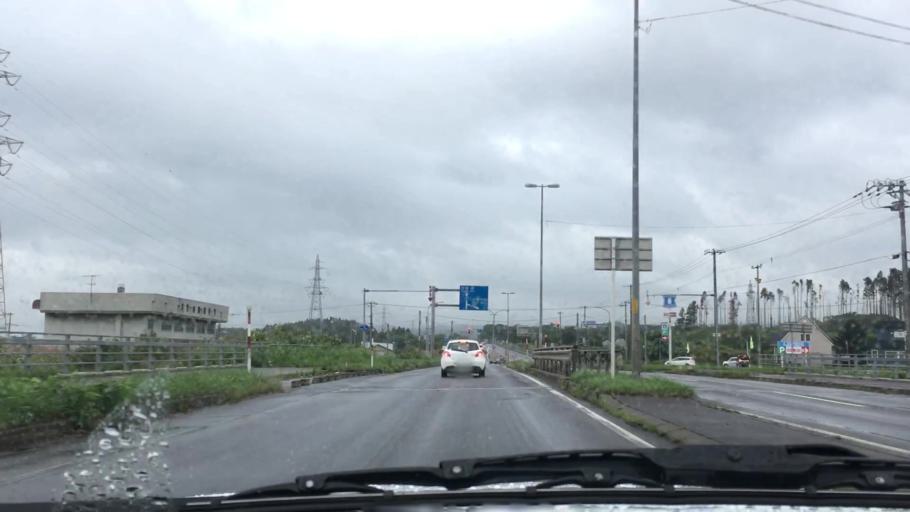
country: JP
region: Hokkaido
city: Nanae
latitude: 42.2470
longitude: 140.2888
